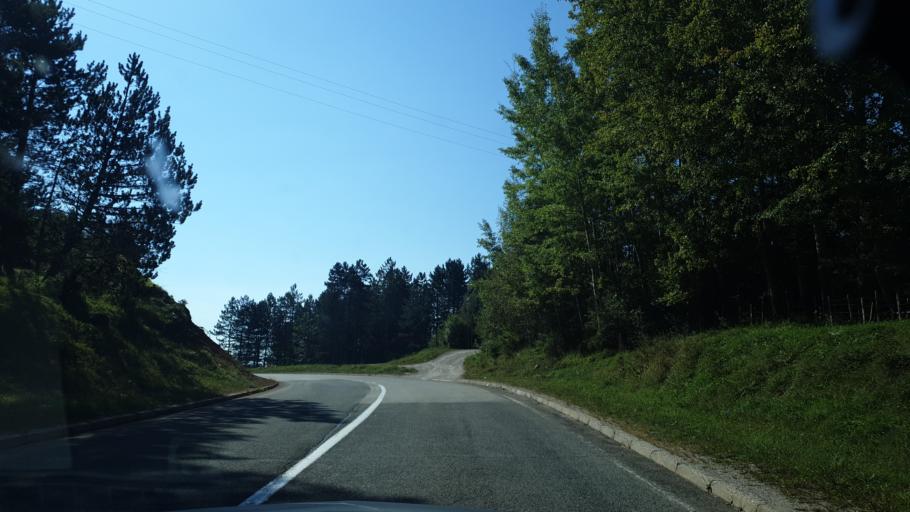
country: RS
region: Central Serbia
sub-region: Zlatiborski Okrug
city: Nova Varos
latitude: 43.5411
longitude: 19.7886
